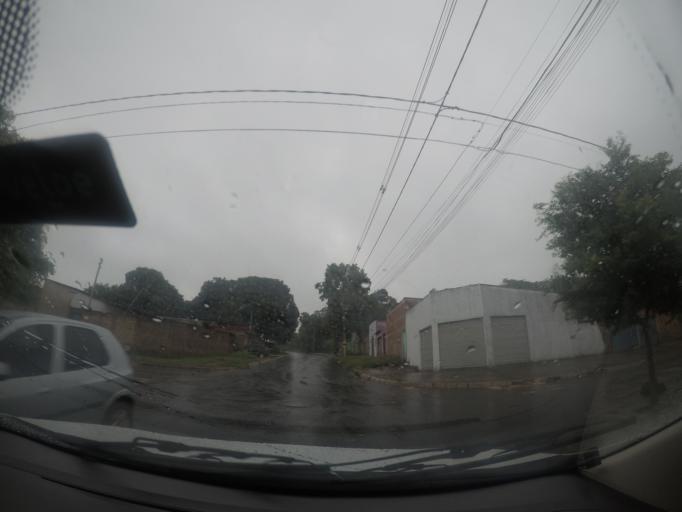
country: BR
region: Goias
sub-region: Goianira
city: Goianira
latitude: -16.5878
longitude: -49.3420
